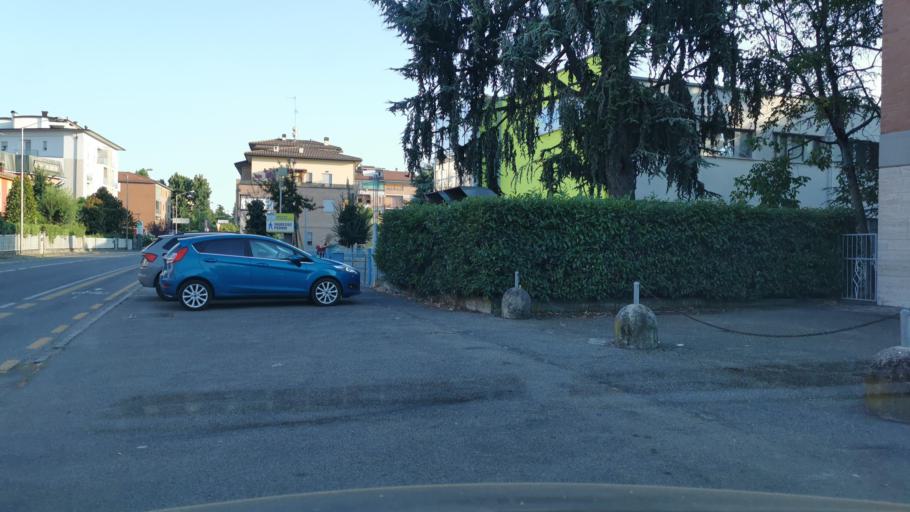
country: IT
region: Emilia-Romagna
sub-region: Provincia di Modena
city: Modena
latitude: 44.6264
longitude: 10.9271
